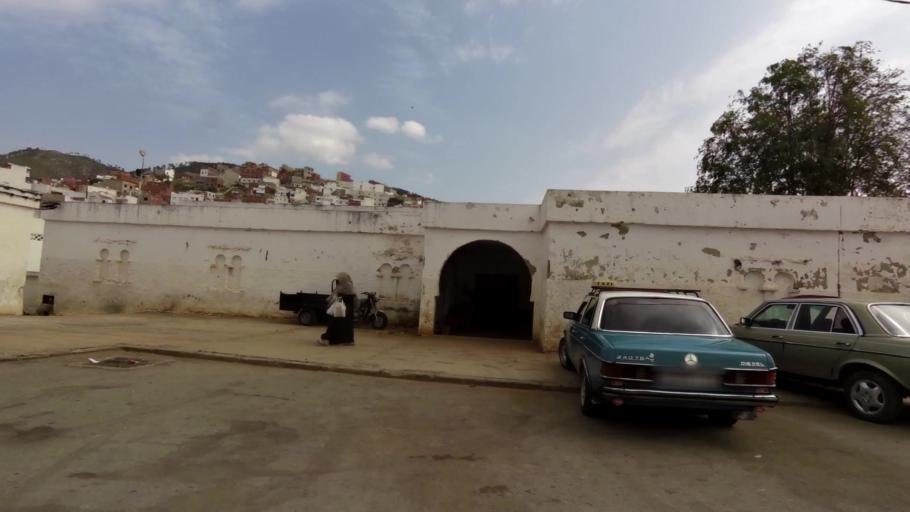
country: MA
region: Tanger-Tetouan
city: Tetouan
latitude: 35.5744
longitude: -5.3964
